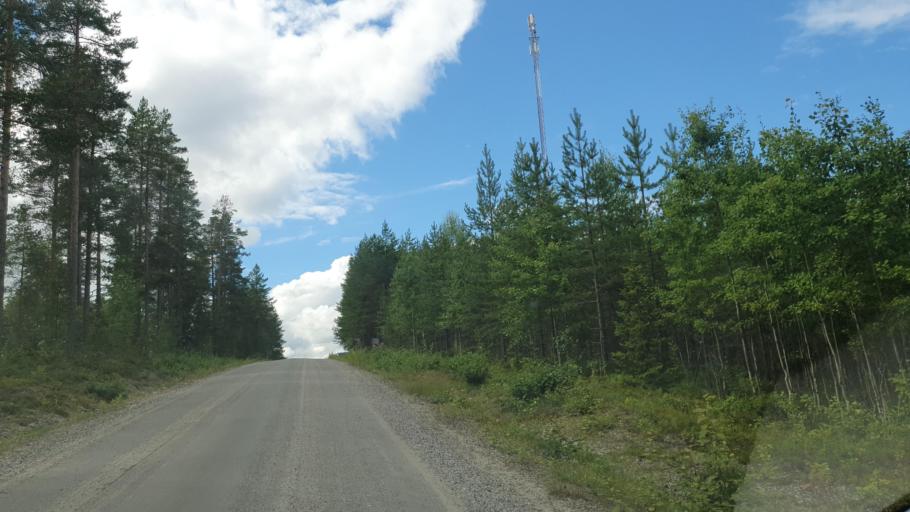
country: FI
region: Kainuu
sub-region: Kehys-Kainuu
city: Kuhmo
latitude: 64.1075
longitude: 29.3454
